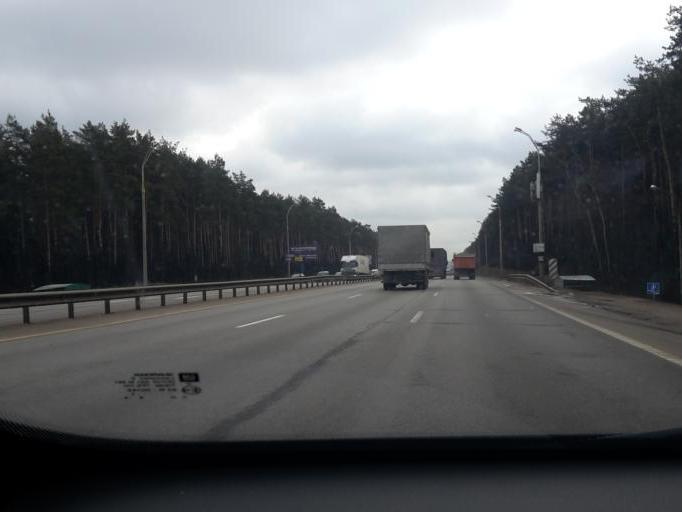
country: BY
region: Minsk
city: Borovlyany
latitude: 53.9552
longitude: 27.6397
